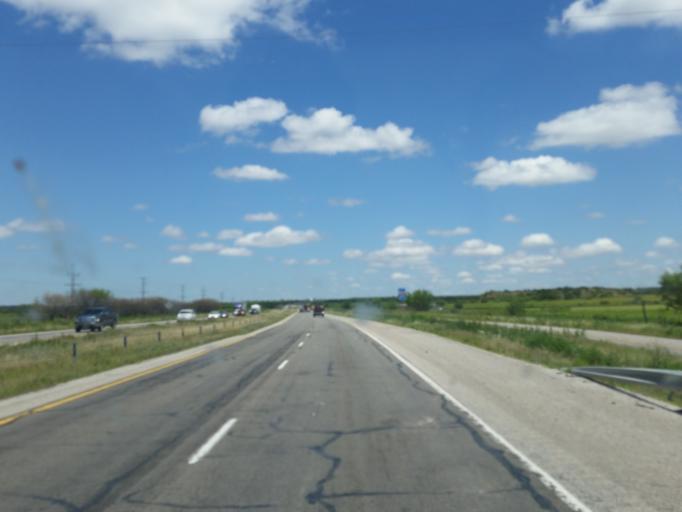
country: US
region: Texas
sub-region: Nolan County
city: Sweetwater
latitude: 32.4944
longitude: -100.2920
